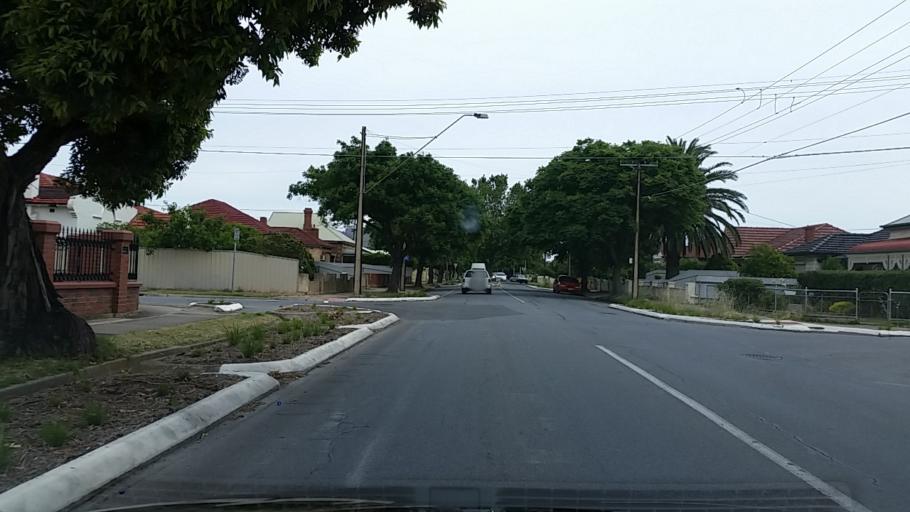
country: AU
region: South Australia
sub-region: Charles Sturt
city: Woodville
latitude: -34.8882
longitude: 138.5599
